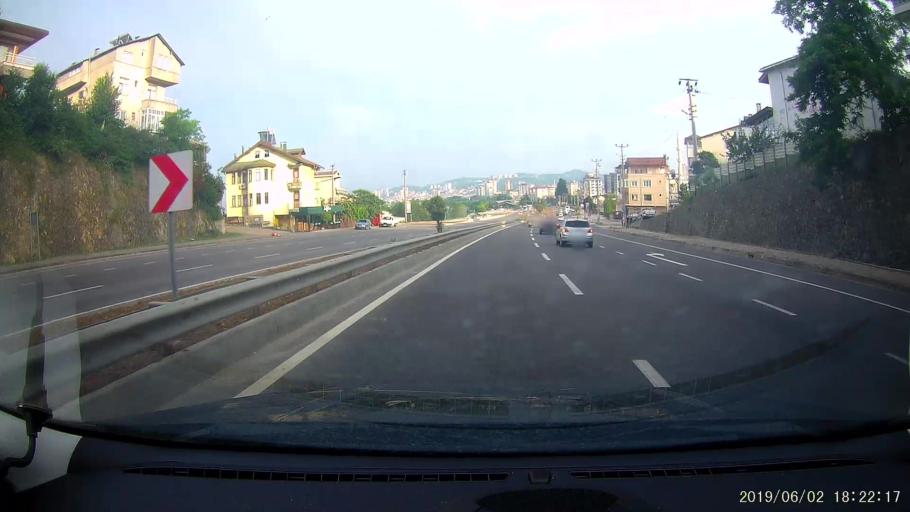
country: TR
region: Ordu
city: Fatsa
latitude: 41.0590
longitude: 37.4766
